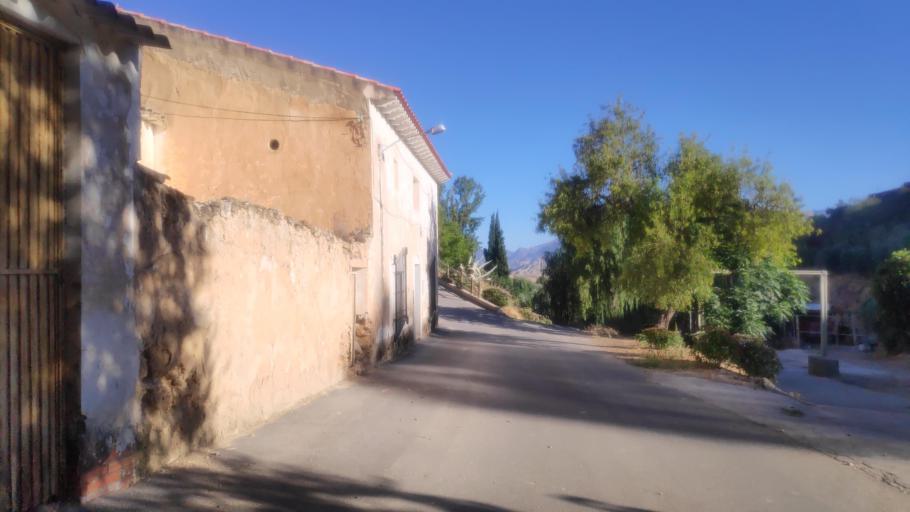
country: ES
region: Andalusia
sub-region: Provincia de Jaen
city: Hinojares
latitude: 37.6753
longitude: -2.9732
